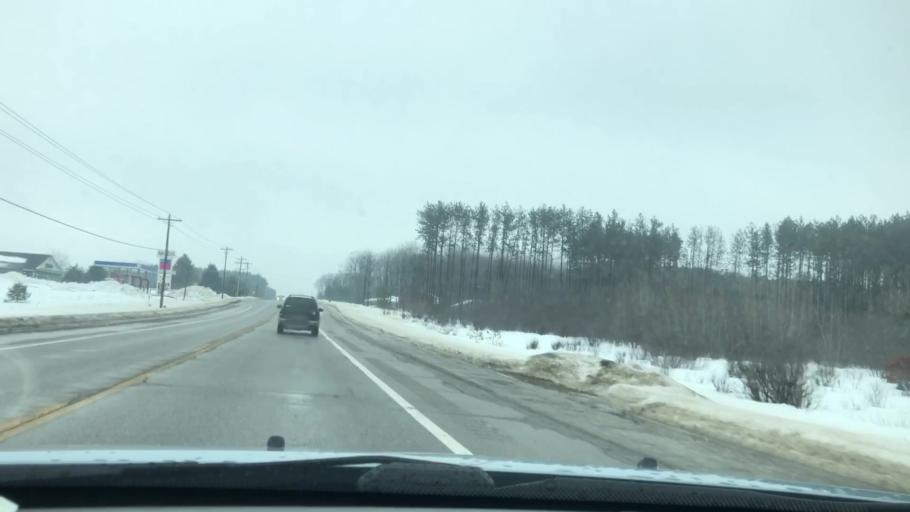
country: US
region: Michigan
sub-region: Otsego County
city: Gaylord
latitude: 45.0276
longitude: -84.7421
